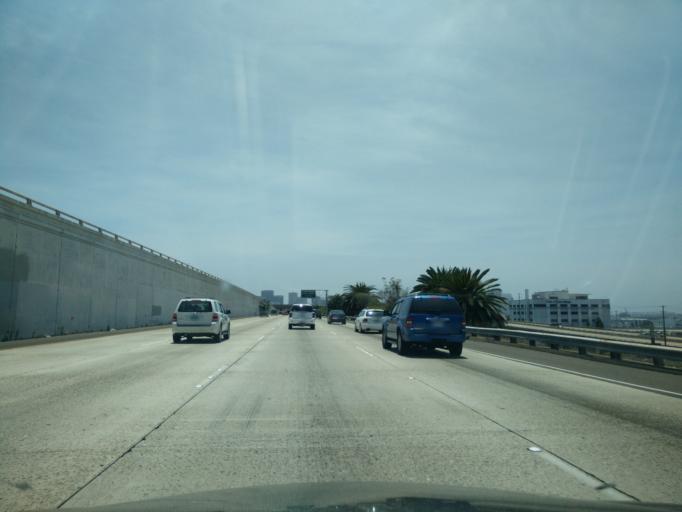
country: US
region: California
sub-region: San Diego County
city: San Diego
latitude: 32.7387
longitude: -117.1780
